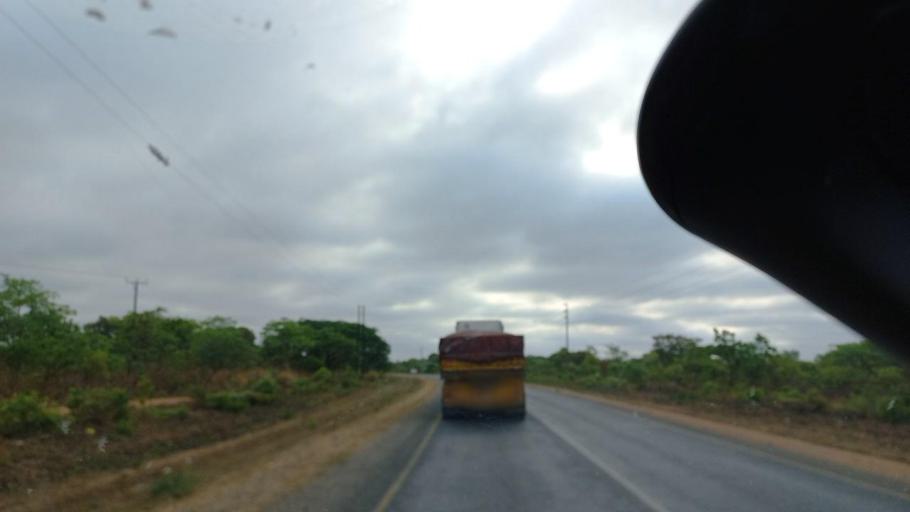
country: ZM
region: Lusaka
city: Chongwe
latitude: -15.3531
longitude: 28.5459
